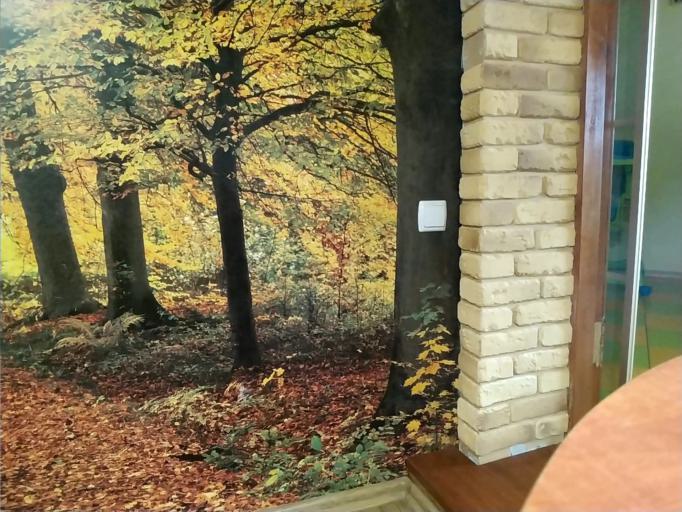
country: RU
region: Smolensk
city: Dorogobuzh
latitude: 54.8992
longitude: 33.3193
